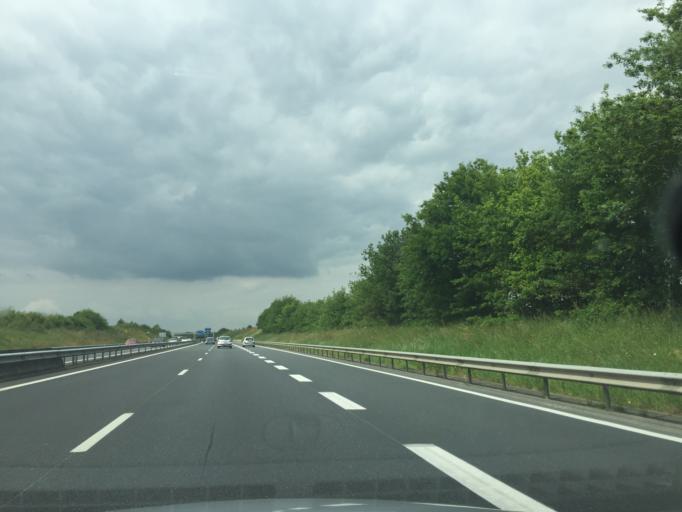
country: FR
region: Pays de la Loire
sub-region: Departement de la Vendee
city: Les Essarts
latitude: 46.7987
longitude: -1.2015
